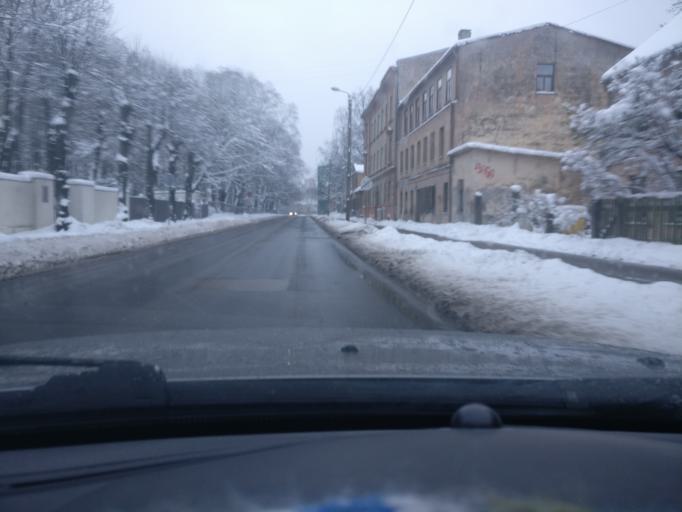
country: LV
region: Riga
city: Riga
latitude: 56.9282
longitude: 24.0862
